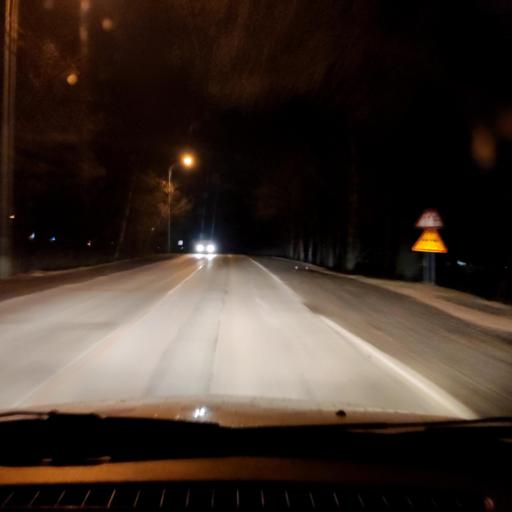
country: RU
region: Bashkortostan
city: Avdon
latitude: 54.7192
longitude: 55.8087
